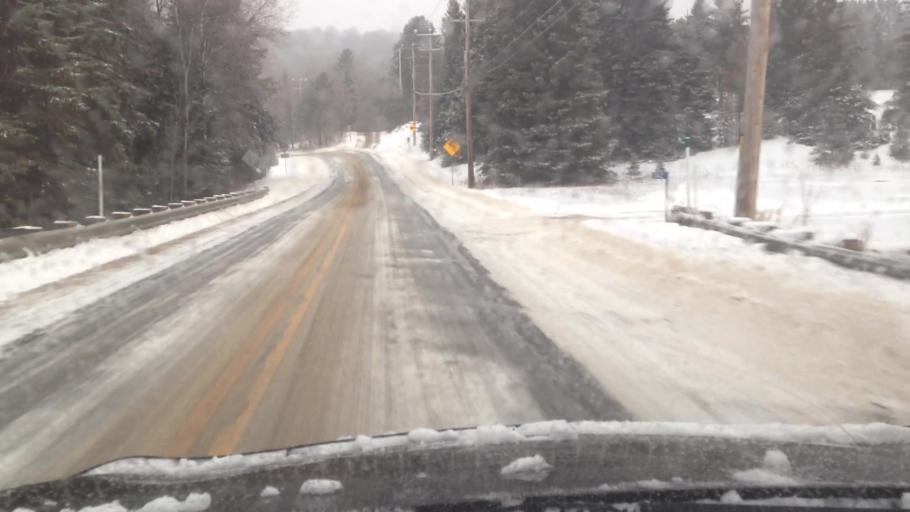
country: CA
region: Quebec
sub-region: Laurentides
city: Mont-Tremblant
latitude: 45.9863
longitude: -74.6110
